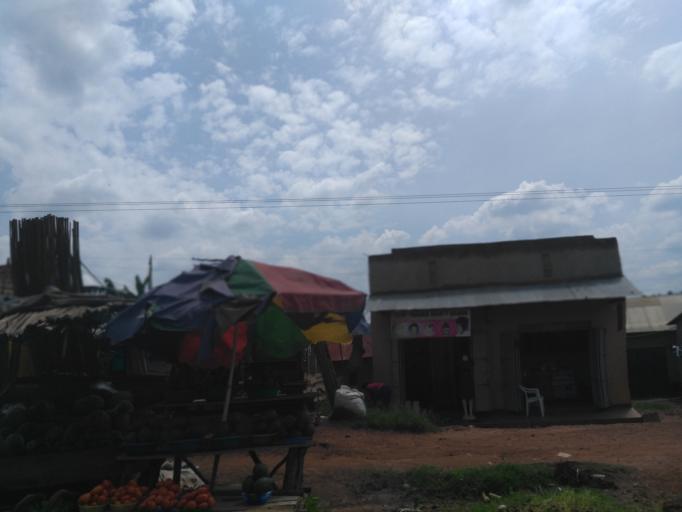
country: UG
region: Central Region
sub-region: Wakiso District
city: Bweyogerere
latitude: 0.4901
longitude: 32.6112
